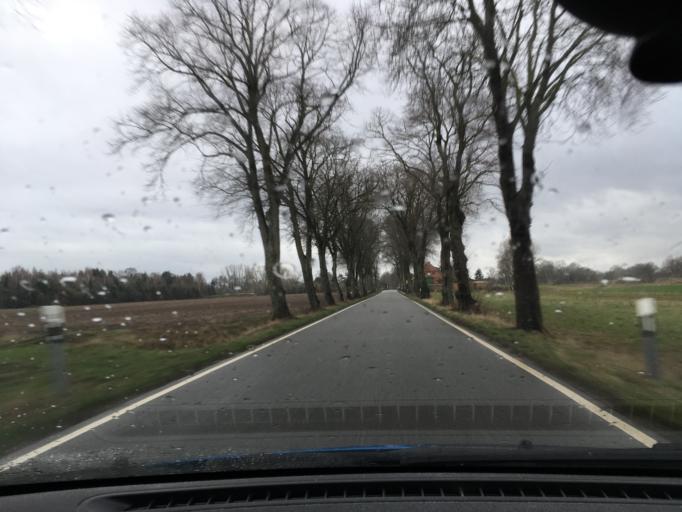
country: DE
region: Lower Saxony
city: Hittbergen
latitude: 53.3515
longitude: 10.6001
